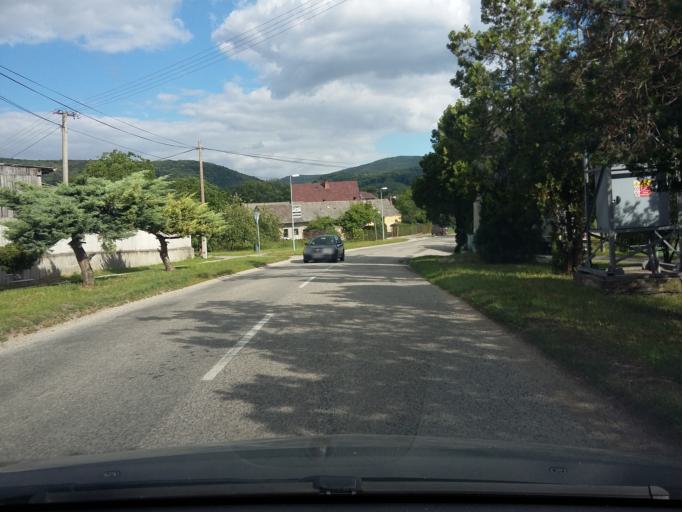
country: SK
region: Trnavsky
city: Smolenice
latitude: 48.5617
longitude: 17.3447
